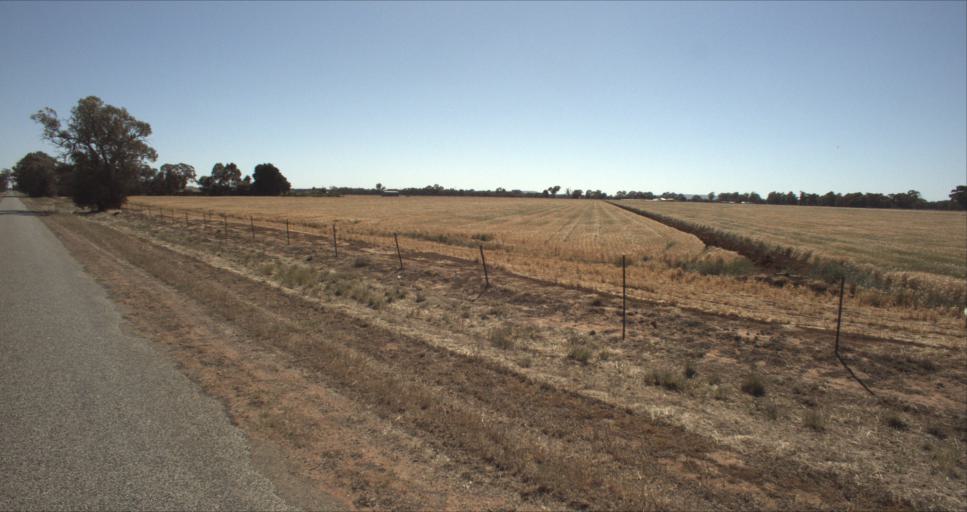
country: AU
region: New South Wales
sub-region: Leeton
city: Leeton
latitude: -34.5474
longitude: 146.3153
